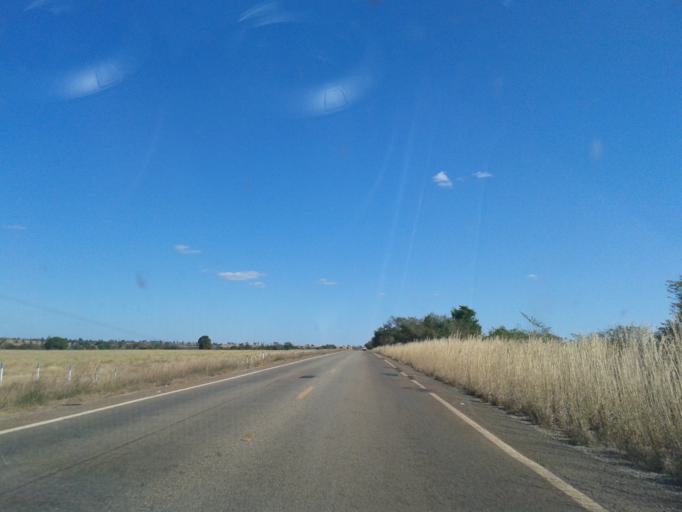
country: BR
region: Goias
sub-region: Mozarlandia
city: Mozarlandia
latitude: -14.3647
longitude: -50.4281
